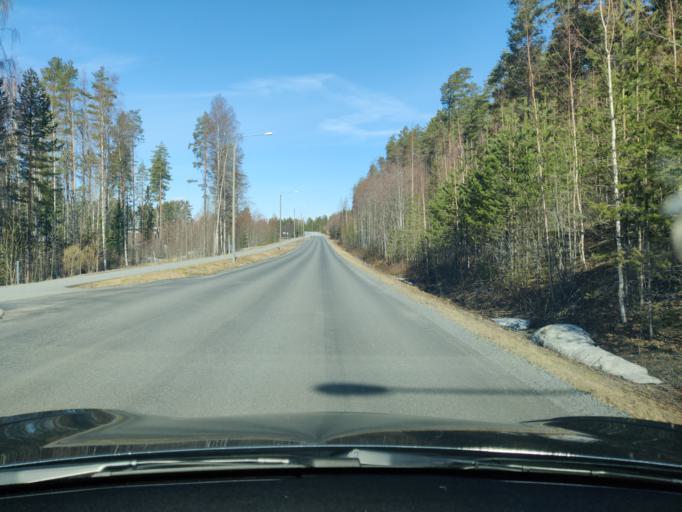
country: FI
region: Northern Savo
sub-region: Kuopio
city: Vehmersalmi
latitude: 62.7676
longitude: 28.0120
